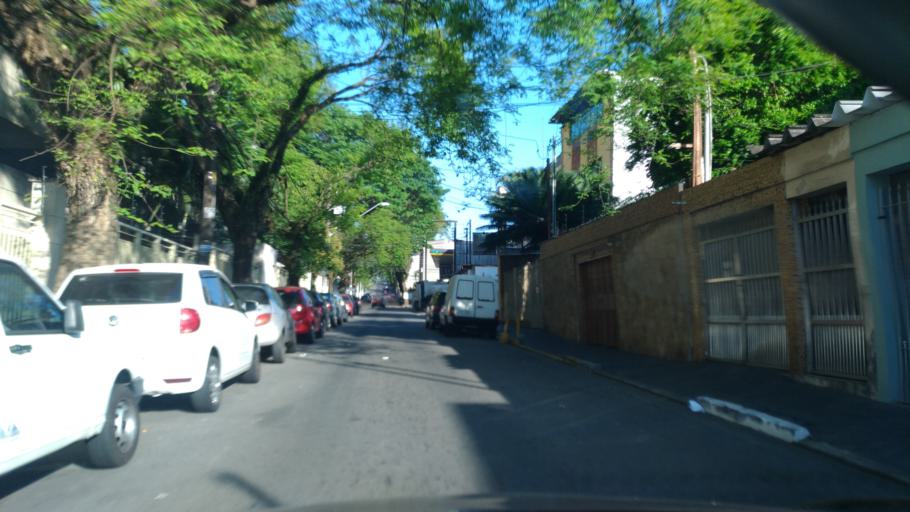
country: BR
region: Sao Paulo
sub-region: Sao Bernardo Do Campo
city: Sao Bernardo do Campo
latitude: -23.6700
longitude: -46.5881
